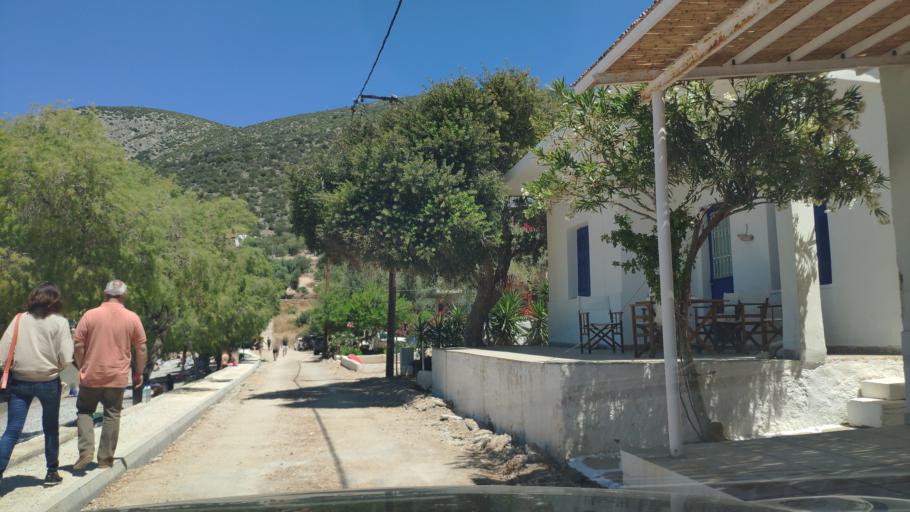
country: GR
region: Central Greece
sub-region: Nomos Voiotias
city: Kaparellion
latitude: 38.1826
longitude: 23.1431
